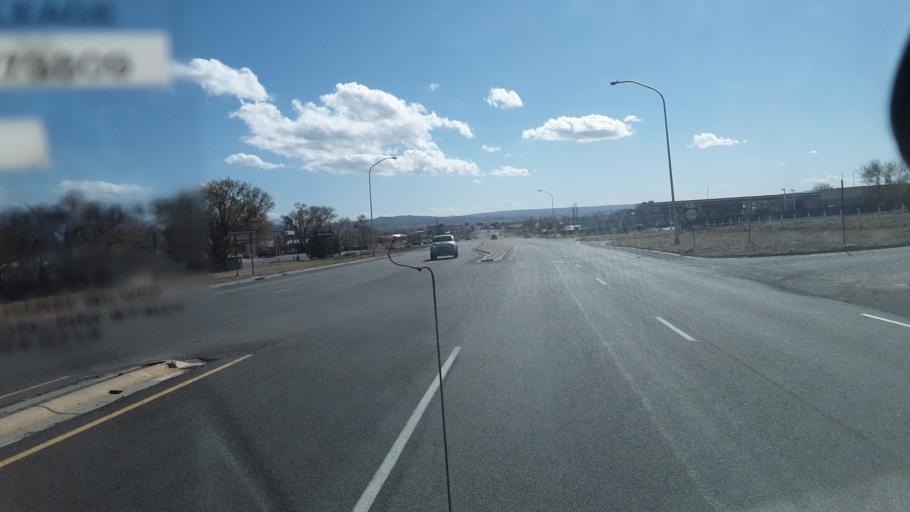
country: US
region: New Mexico
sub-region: Rio Arriba County
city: Espanola
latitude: 36.0107
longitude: -106.0886
